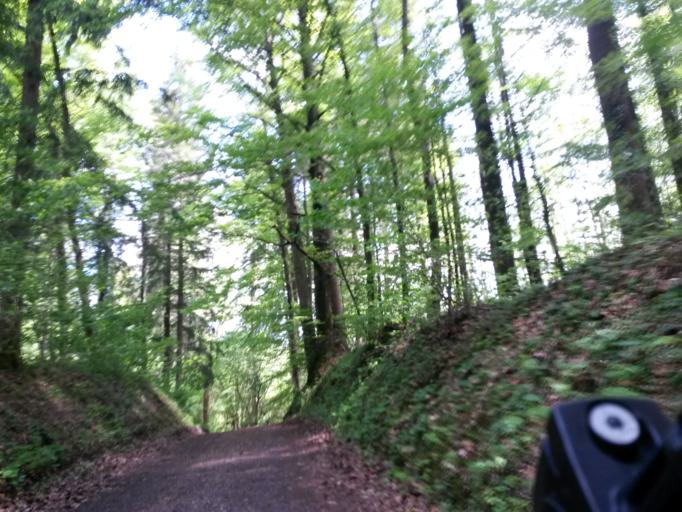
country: DE
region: Baden-Wuerttemberg
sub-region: Tuebingen Region
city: Bad Waldsee
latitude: 47.9010
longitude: 9.7417
